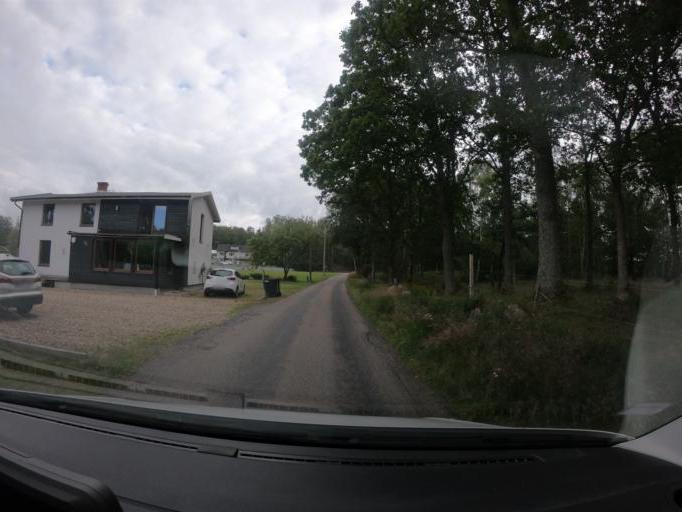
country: SE
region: Skane
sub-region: Angelholms Kommun
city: Munka-Ljungby
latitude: 56.3297
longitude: 12.9759
